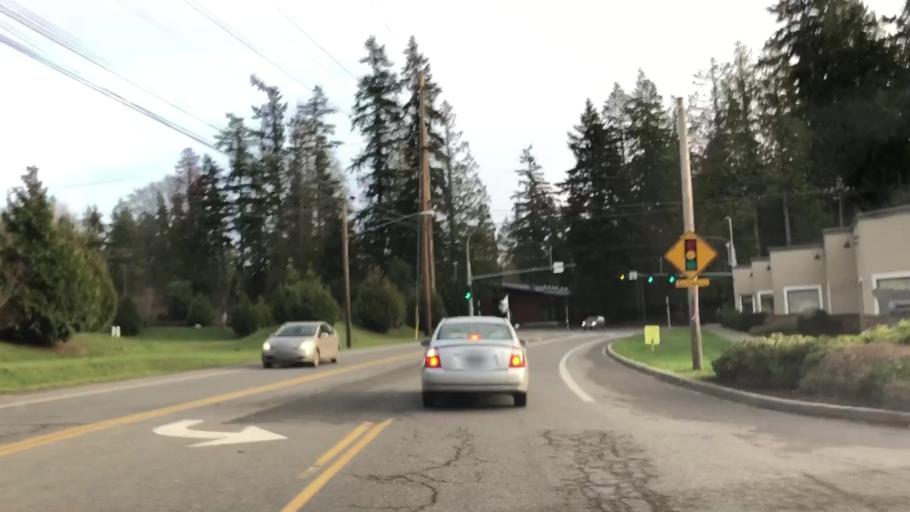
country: US
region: Washington
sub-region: Kitsap County
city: Suquamish
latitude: 47.7288
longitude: -122.5594
